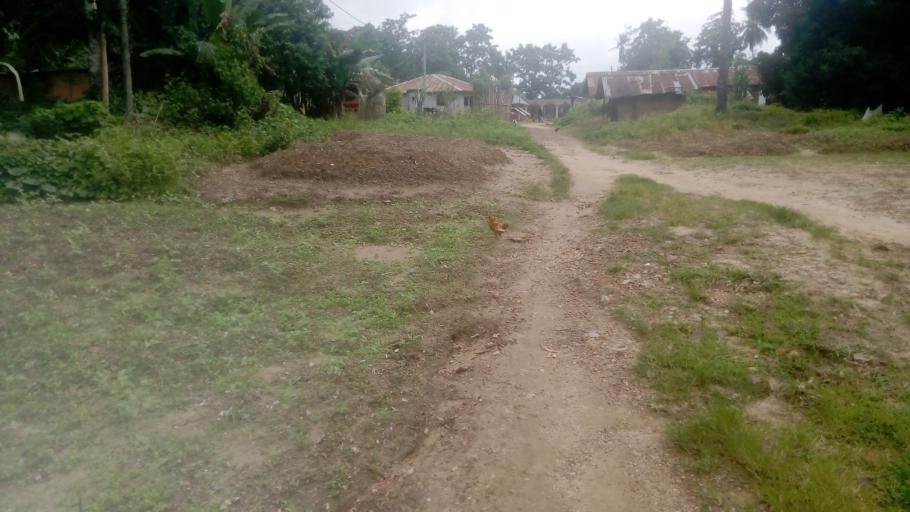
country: SL
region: Northern Province
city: Lunsar
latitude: 8.6814
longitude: -12.5523
